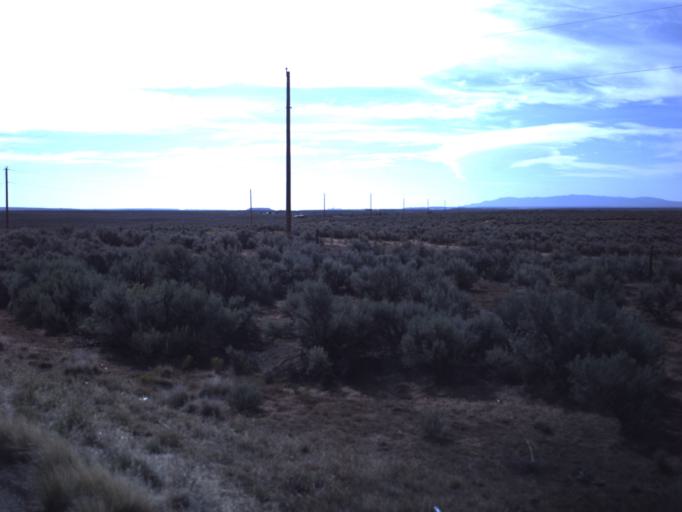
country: US
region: Utah
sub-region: San Juan County
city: Blanding
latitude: 37.4297
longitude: -109.3604
